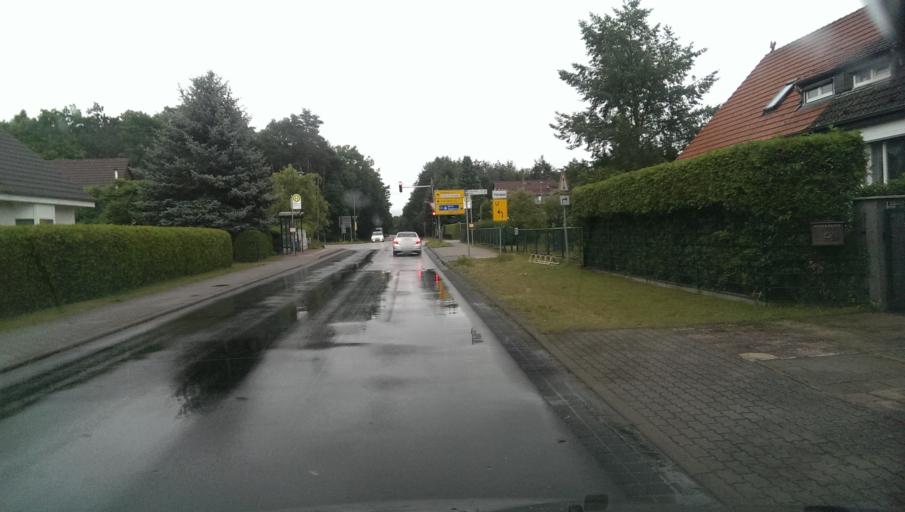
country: DE
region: Brandenburg
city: Gross Kreutz
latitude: 52.3618
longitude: 12.7645
